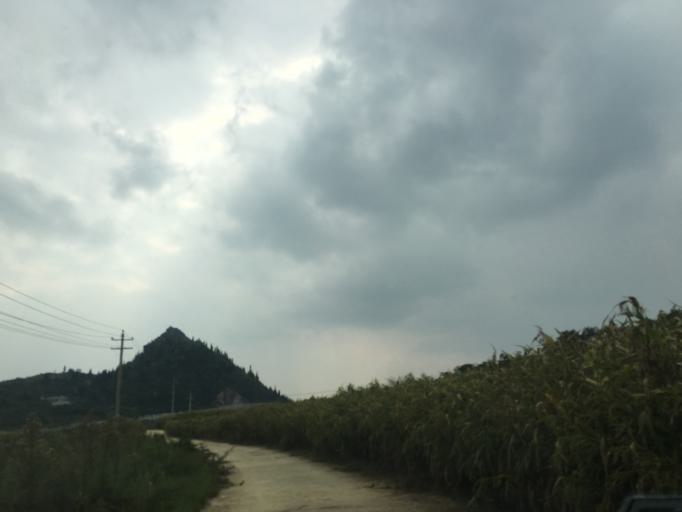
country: CN
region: Guangxi Zhuangzu Zizhiqu
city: Xinzhou
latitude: 25.4854
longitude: 105.6489
